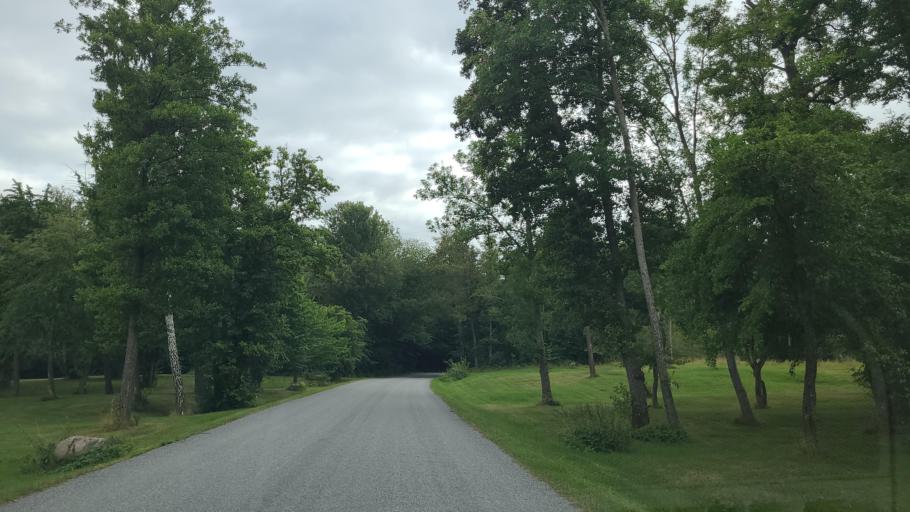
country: SE
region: Stockholm
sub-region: Upplands-Bro Kommun
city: Bro
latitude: 59.4829
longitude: 17.5676
